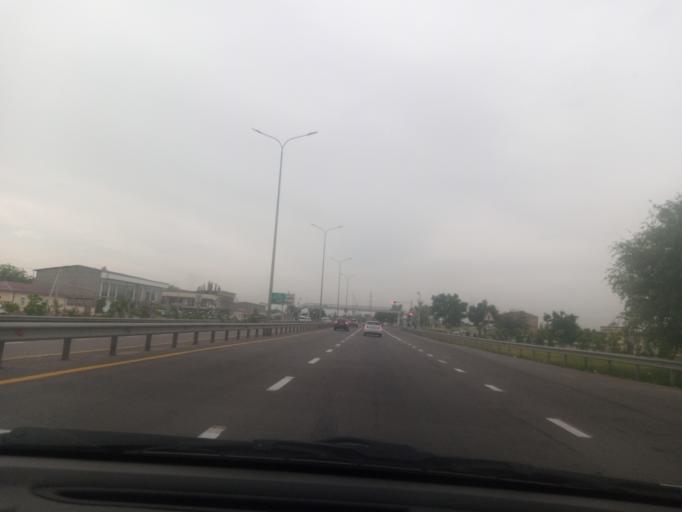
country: UZ
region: Toshkent
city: Tuytepa
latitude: 41.1321
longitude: 69.4358
